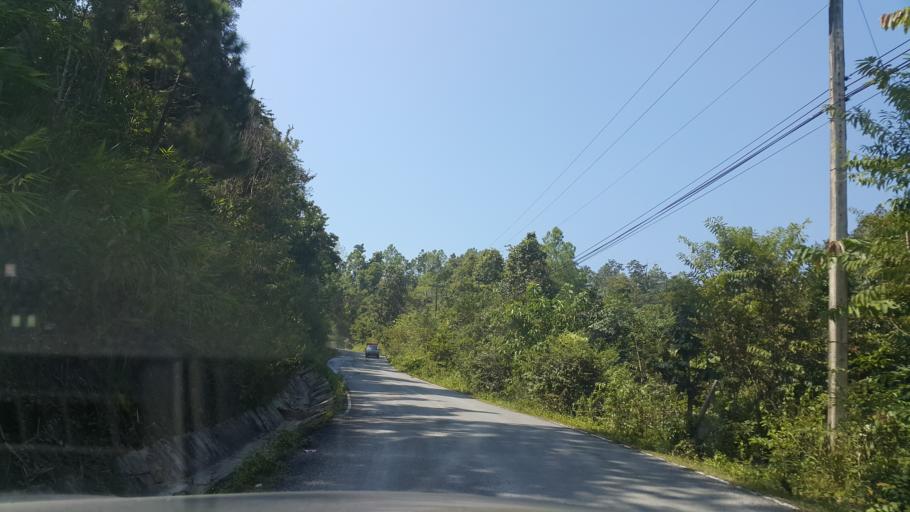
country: TH
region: Chiang Mai
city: Samoeng
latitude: 18.8995
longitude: 98.5983
